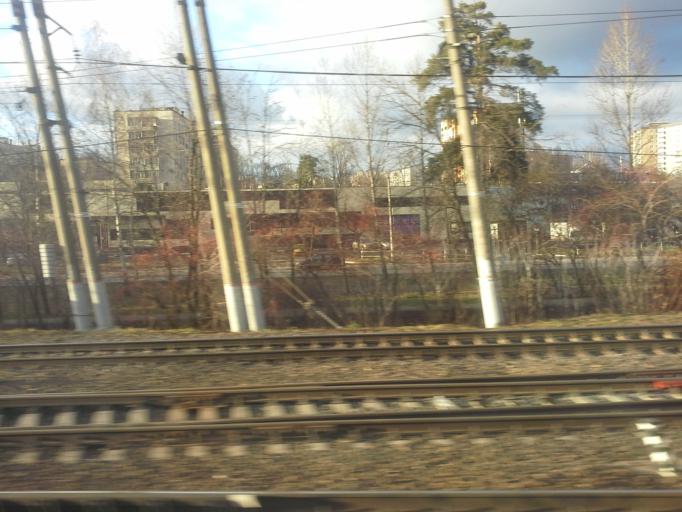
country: RU
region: Moskovskaya
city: Mytishchi
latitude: 55.9226
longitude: 37.7707
